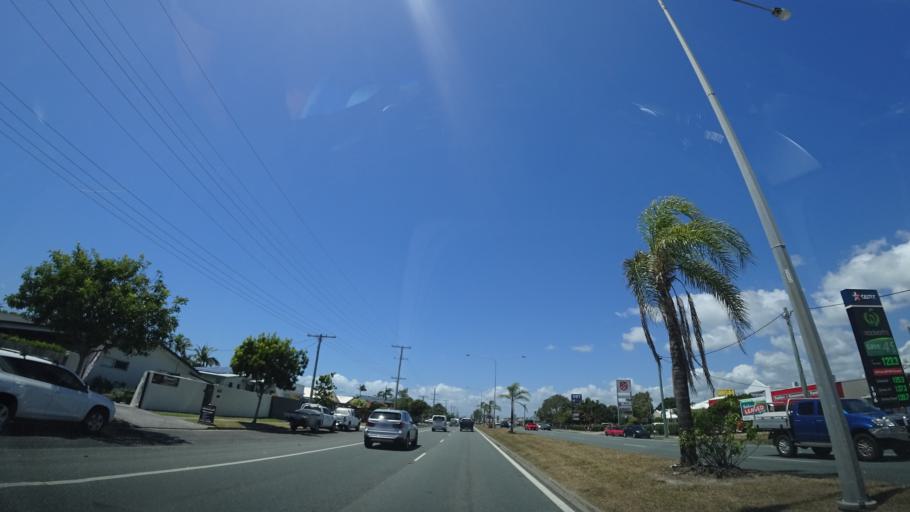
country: AU
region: Queensland
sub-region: Sunshine Coast
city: Mooloolaba
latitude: -26.7214
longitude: 153.1296
